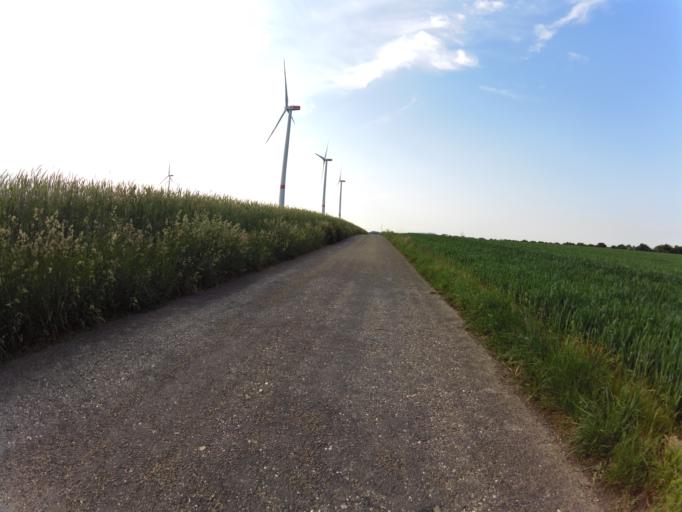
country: DE
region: North Rhine-Westphalia
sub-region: Regierungsbezirk Koln
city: Linnich
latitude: 50.9802
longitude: 6.2022
